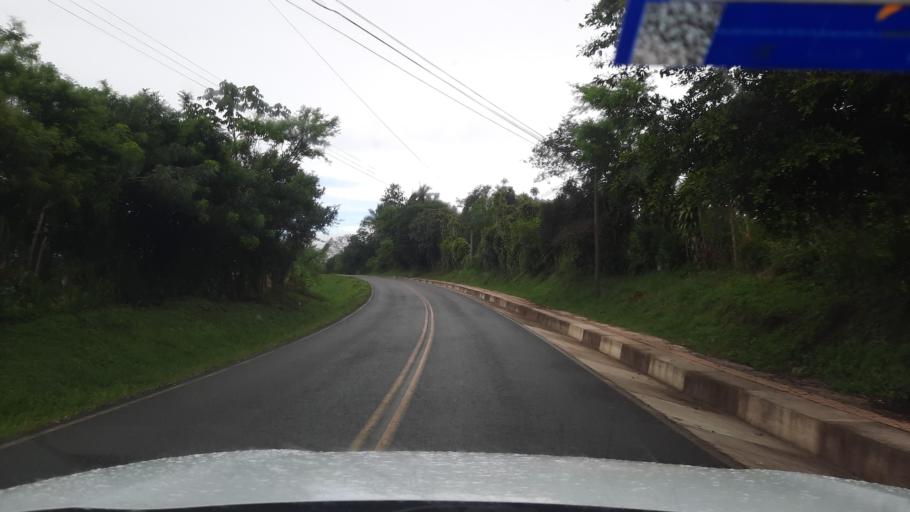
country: PA
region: Chiriqui
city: Rio Sereno
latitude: 8.8174
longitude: -82.8648
